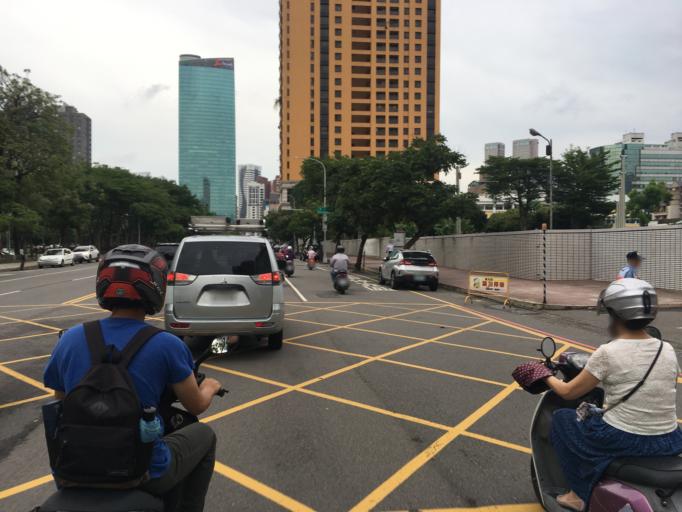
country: TW
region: Taiwan
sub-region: Taichung City
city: Taichung
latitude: 24.1448
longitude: 120.6654
